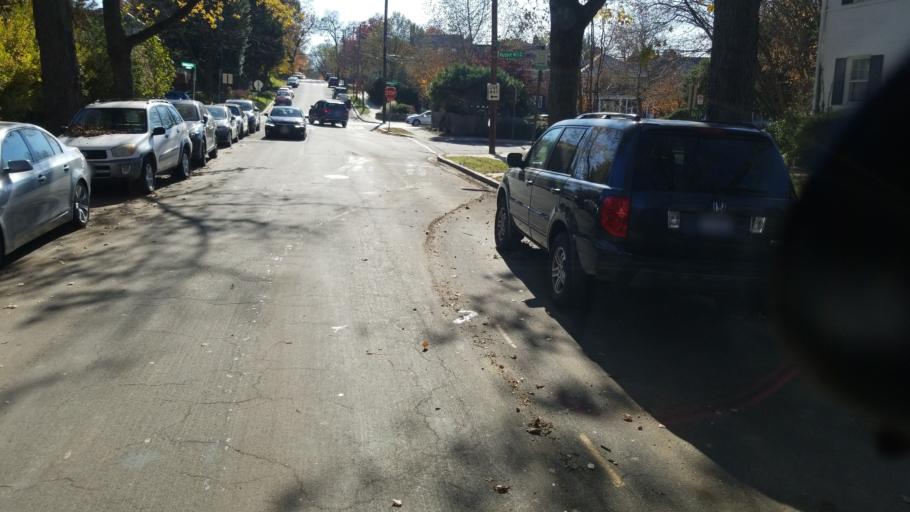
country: US
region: Maryland
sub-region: Montgomery County
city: Friendship Village
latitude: 38.9485
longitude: -77.0838
